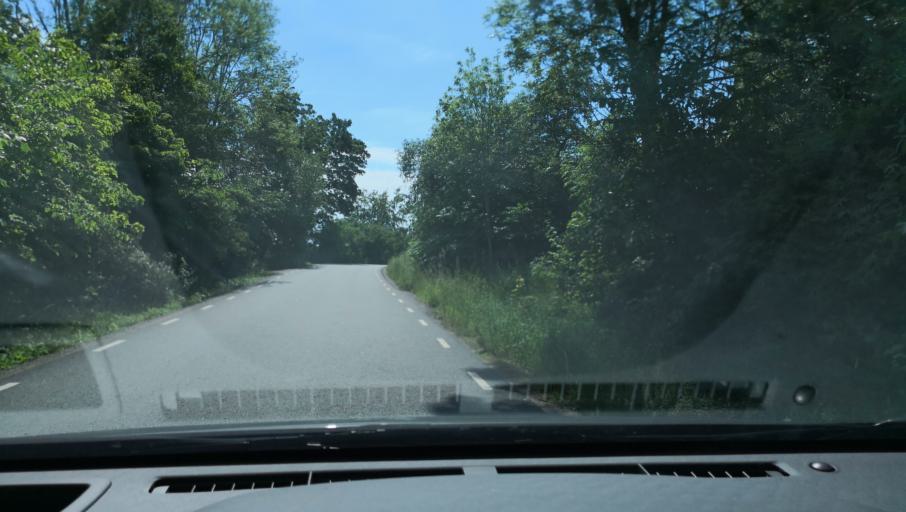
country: SE
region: Uppsala
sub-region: Habo Kommun
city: Balsta
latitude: 59.6716
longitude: 17.4630
